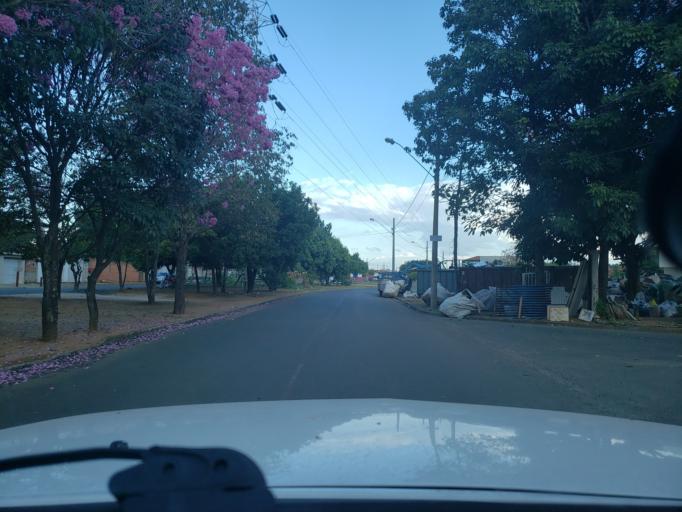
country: BR
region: Sao Paulo
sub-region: Moji-Guacu
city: Mogi-Gaucu
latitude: -22.3271
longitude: -46.9212
